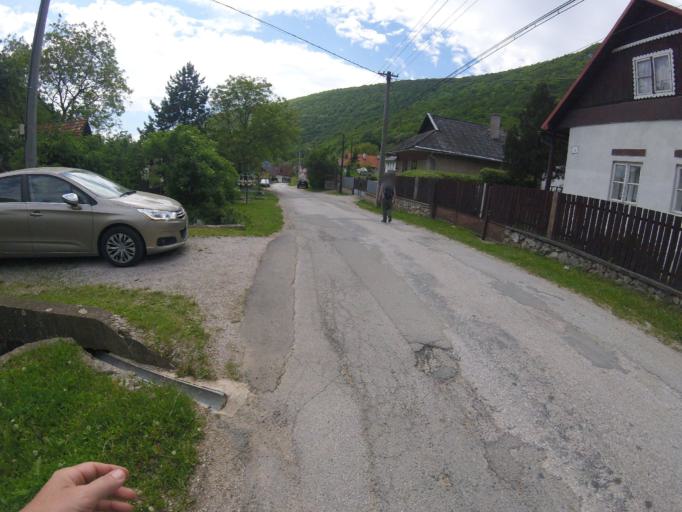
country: SK
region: Kosicky
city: Medzev
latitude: 48.6333
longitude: 20.8503
